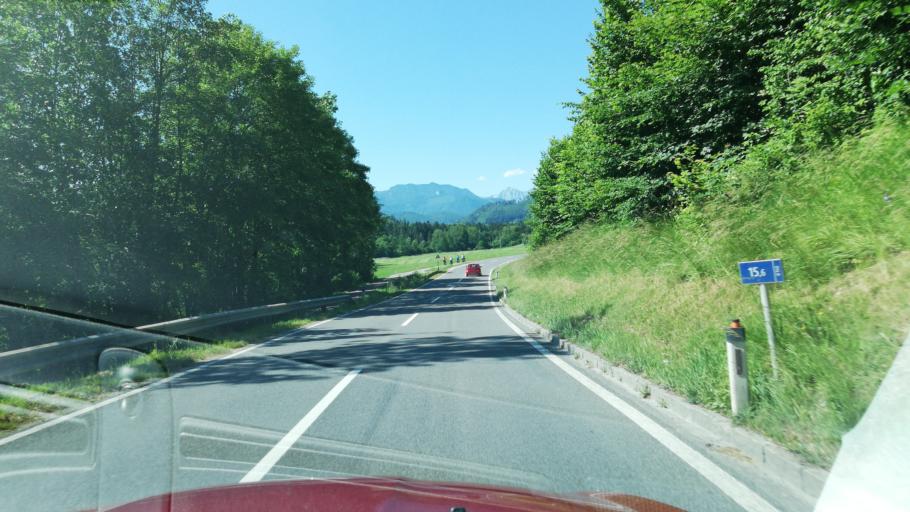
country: AT
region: Upper Austria
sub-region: Politischer Bezirk Kirchdorf an der Krems
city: Gruenburg
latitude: 47.9193
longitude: 14.2450
